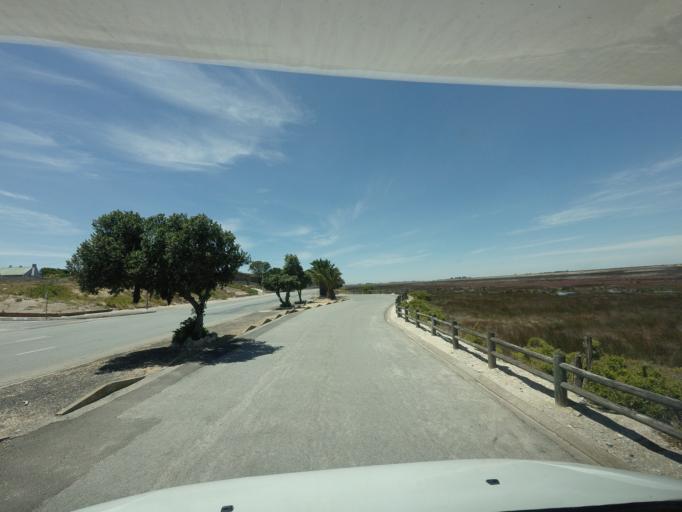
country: ZA
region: Western Cape
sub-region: West Coast District Municipality
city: Vredenburg
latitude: -32.7869
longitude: 18.1748
